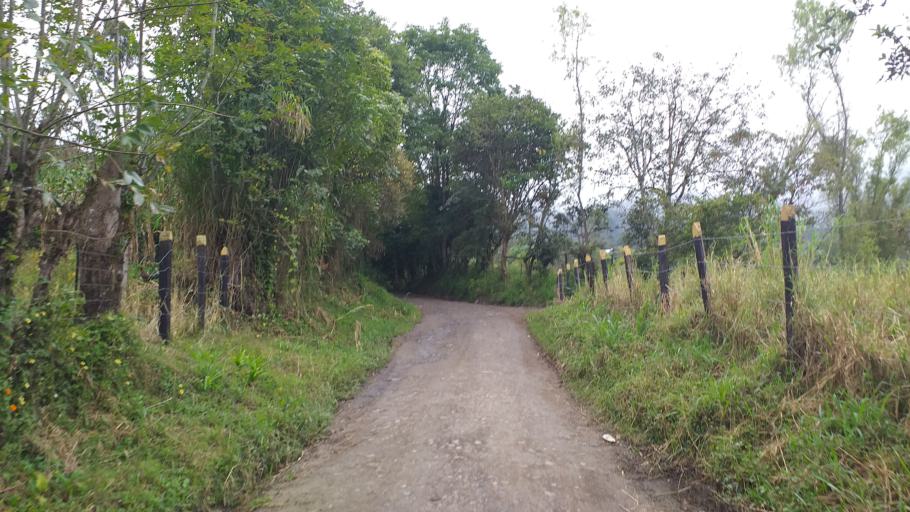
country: CO
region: Cundinamarca
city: Tenza
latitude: 5.1001
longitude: -73.4492
